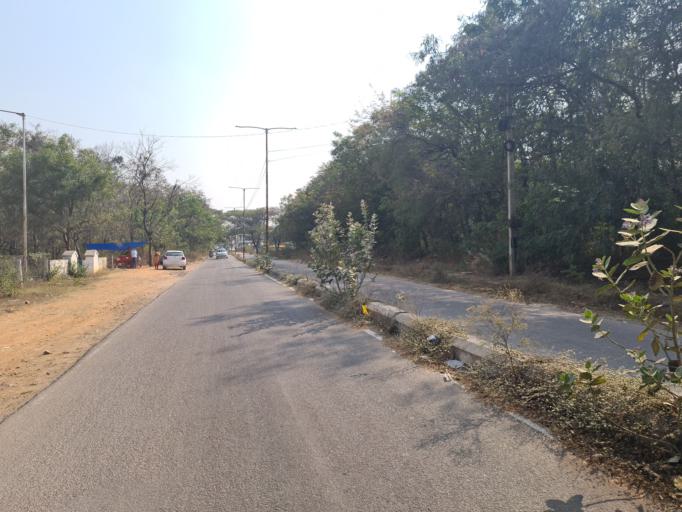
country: IN
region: Telangana
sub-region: Medak
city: Serilingampalle
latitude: 17.4864
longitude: 78.2980
